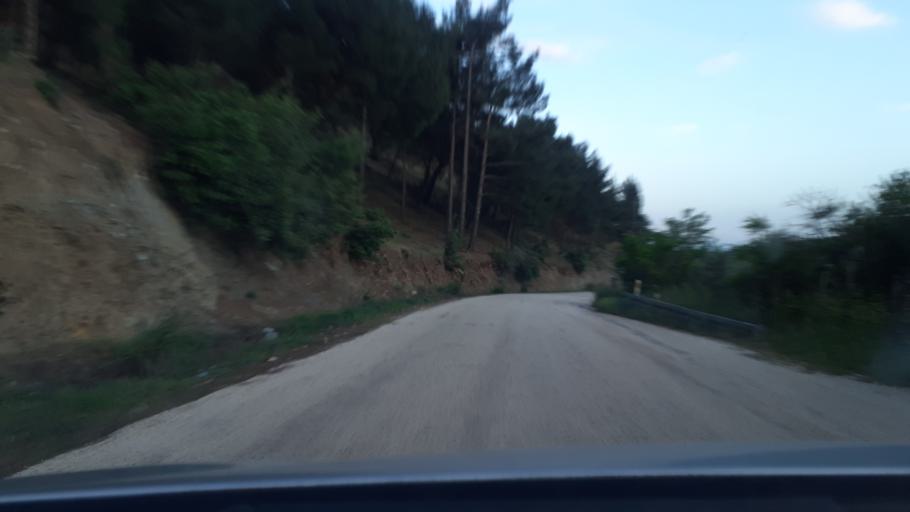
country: TR
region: Hatay
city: Kirikhan
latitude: 36.5190
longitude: 36.3182
